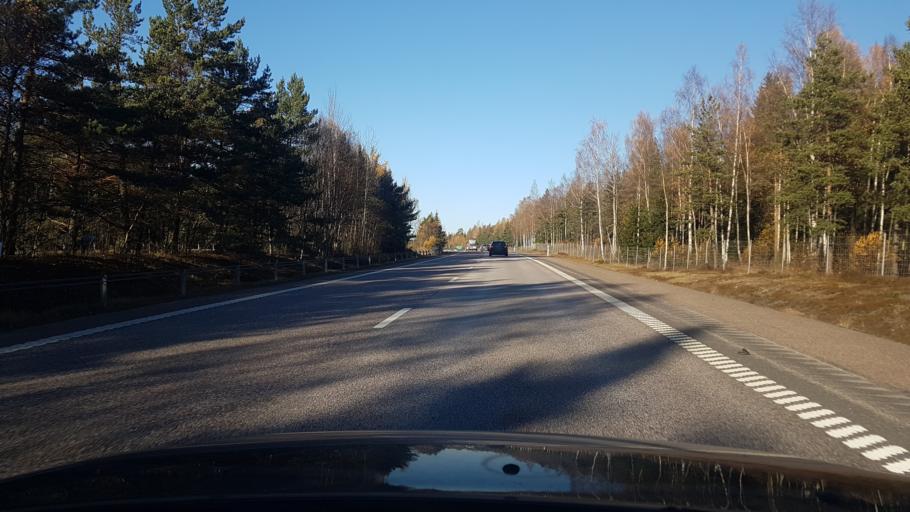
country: SE
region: Stockholm
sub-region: Sigtuna Kommun
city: Marsta
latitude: 59.6944
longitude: 17.8668
